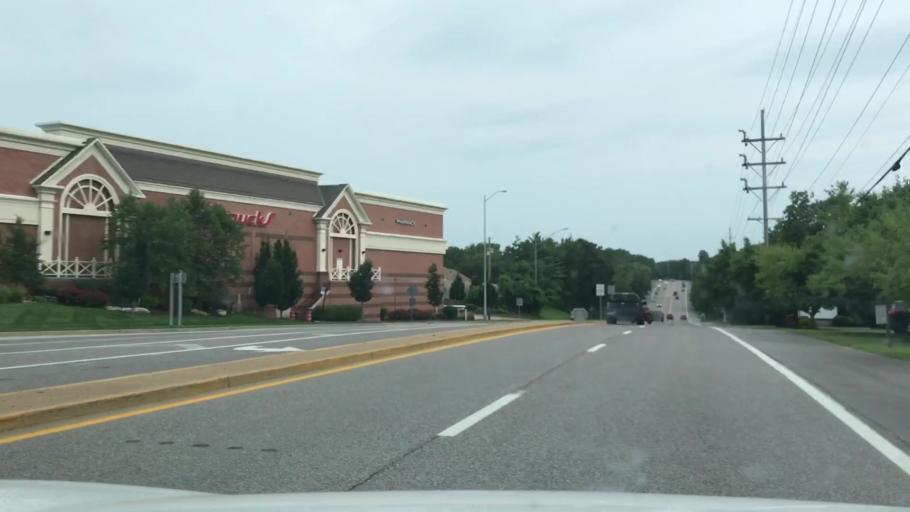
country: US
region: Missouri
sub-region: Saint Louis County
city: Clarkson Valley
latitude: 38.6214
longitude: -90.5822
